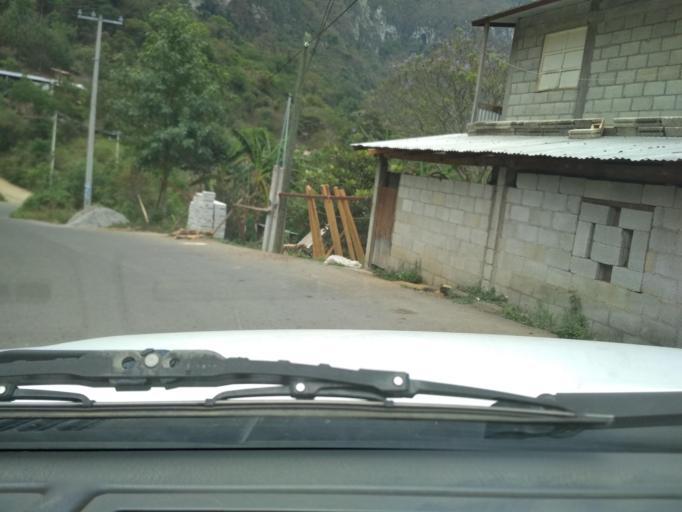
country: MX
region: Veracruz
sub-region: Camerino Z. Mendoza
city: La Cuesta
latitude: 18.7909
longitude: -97.1717
